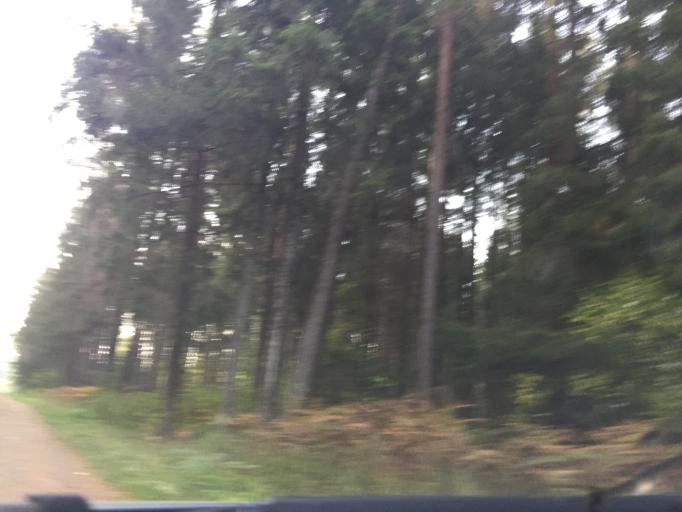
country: LV
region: Ikskile
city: Ikskile
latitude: 56.9289
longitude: 24.4931
